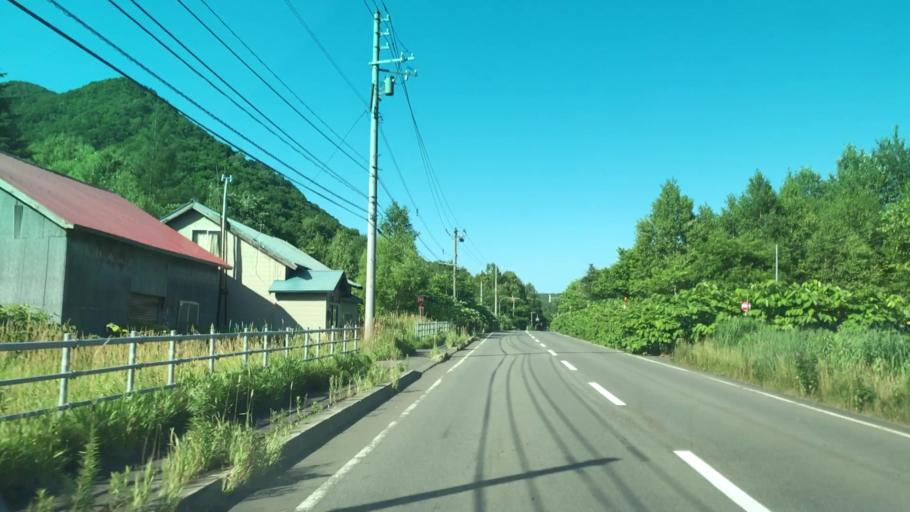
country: JP
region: Hokkaido
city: Yoichi
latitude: 43.0572
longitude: 140.8653
